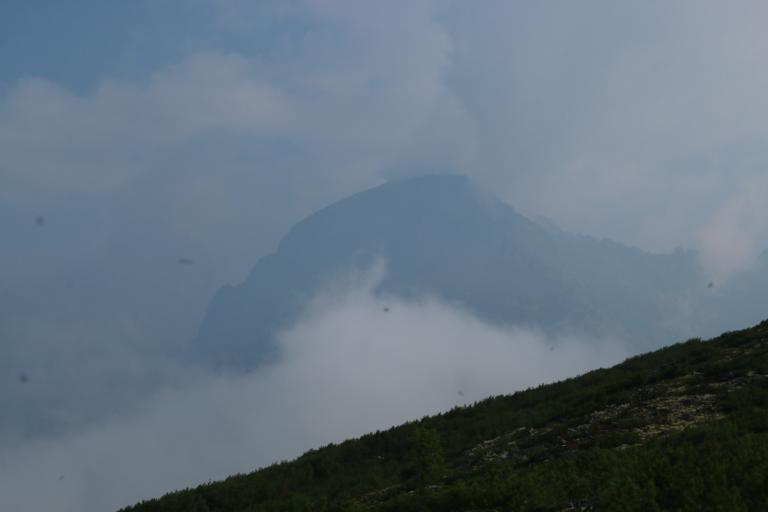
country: RU
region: Respublika Buryatiya
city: Kichera
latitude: 56.3412
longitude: 110.0774
